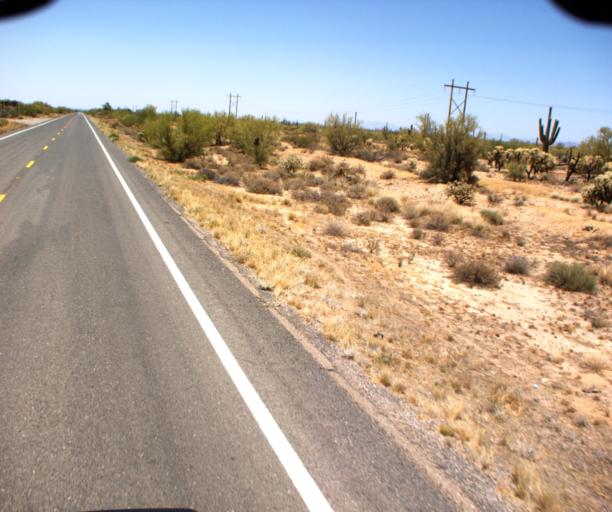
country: US
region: Arizona
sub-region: Pinal County
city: Florence
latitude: 32.8879
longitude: -111.2663
